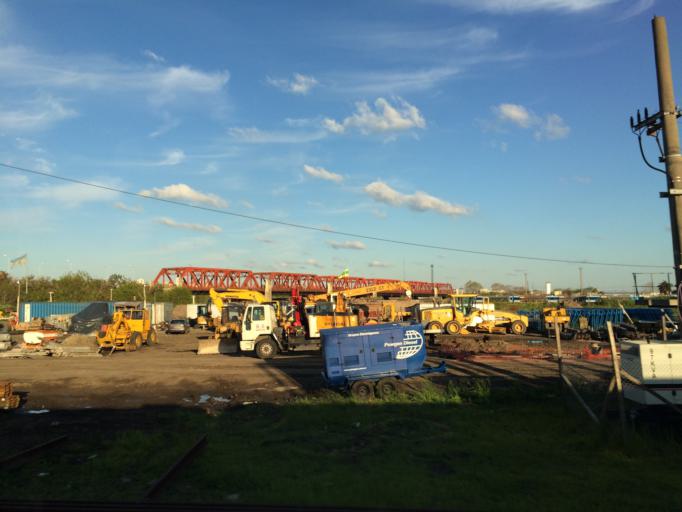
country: AR
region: Buenos Aires
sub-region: Partido de Avellaneda
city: Avellaneda
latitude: -34.6727
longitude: -58.3777
